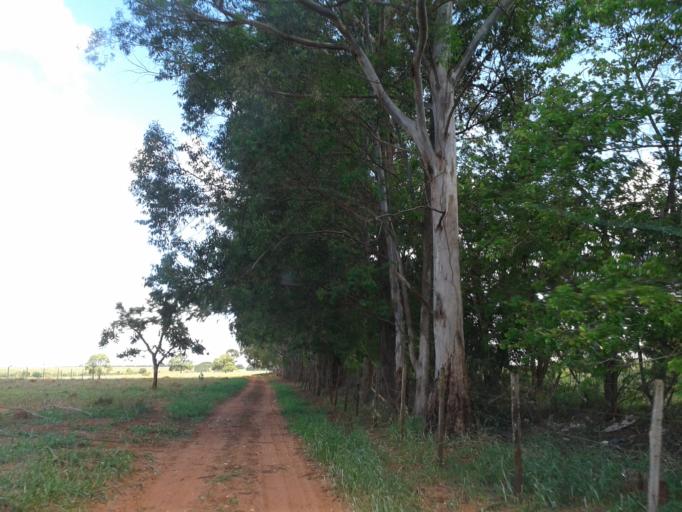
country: BR
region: Minas Gerais
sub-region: Centralina
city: Centralina
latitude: -18.7199
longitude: -49.1587
